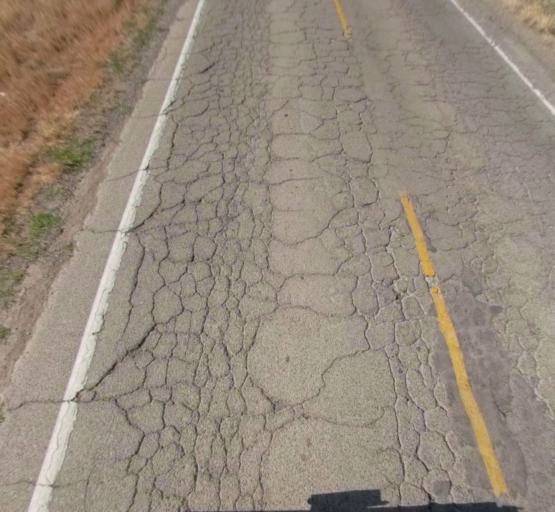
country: US
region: California
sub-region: Madera County
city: Chowchilla
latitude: 37.0657
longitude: -120.2568
